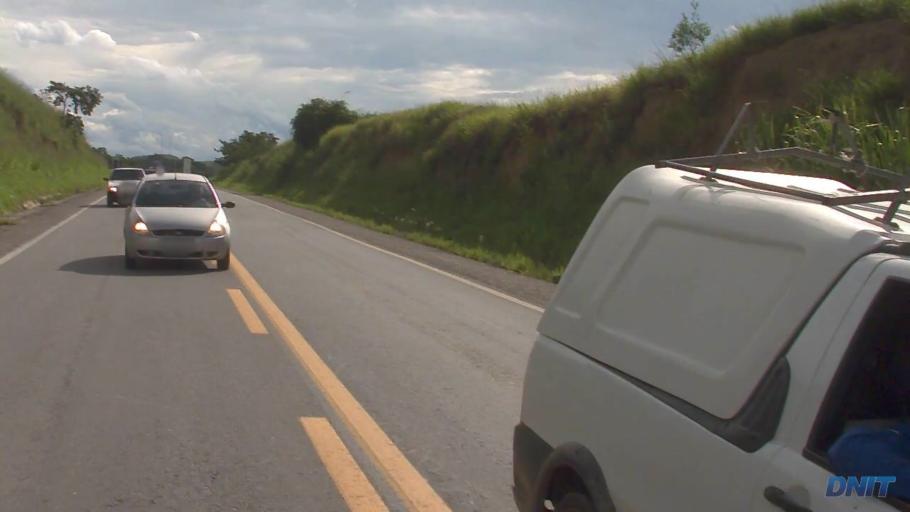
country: BR
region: Minas Gerais
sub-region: Belo Oriente
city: Belo Oriente
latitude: -19.2003
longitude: -42.2877
